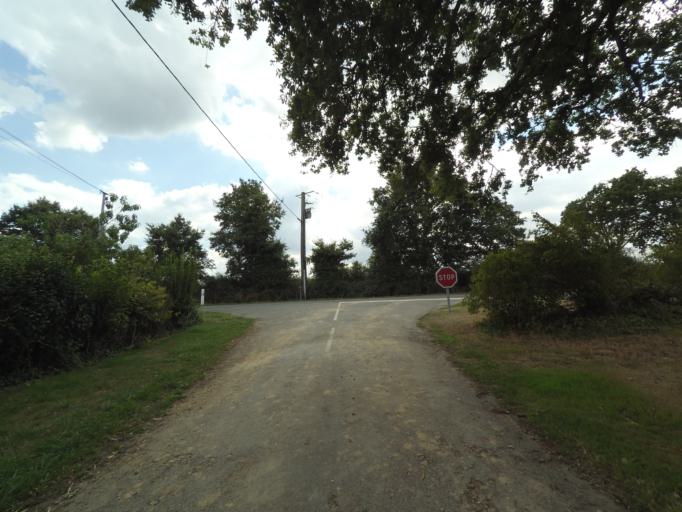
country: FR
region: Pays de la Loire
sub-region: Departement de la Loire-Atlantique
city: Vieillevigne
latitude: 46.9748
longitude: -1.4185
